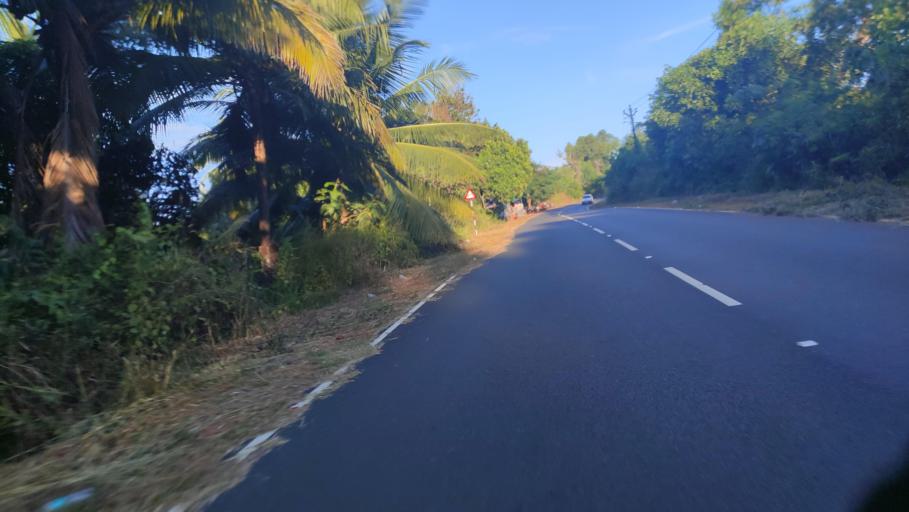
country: IN
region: Kerala
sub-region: Kasaragod District
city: Kasaragod
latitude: 12.4578
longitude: 75.0905
